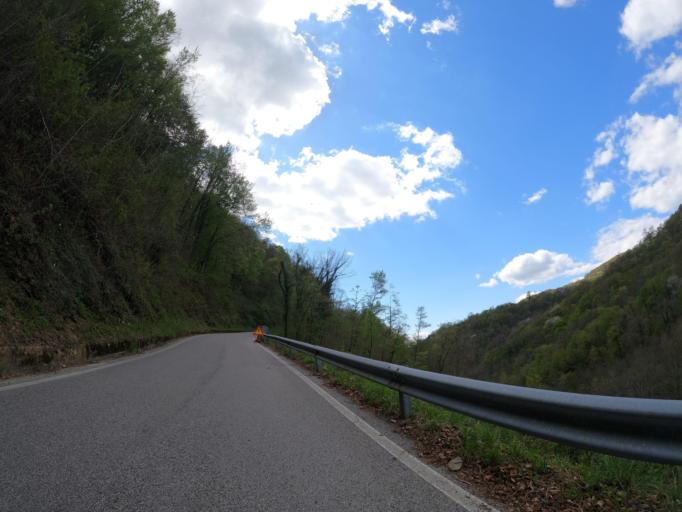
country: IT
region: Friuli Venezia Giulia
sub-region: Provincia di Udine
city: Stregna
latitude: 46.1306
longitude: 13.5764
